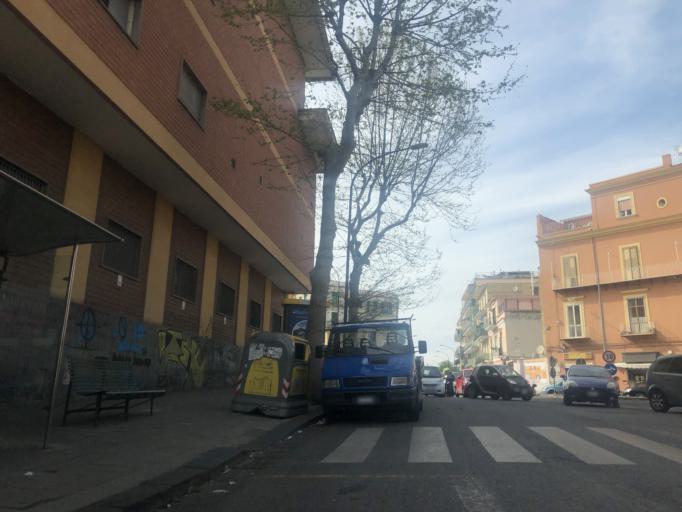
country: IT
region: Campania
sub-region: Provincia di Napoli
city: Napoli
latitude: 40.8636
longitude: 14.2196
